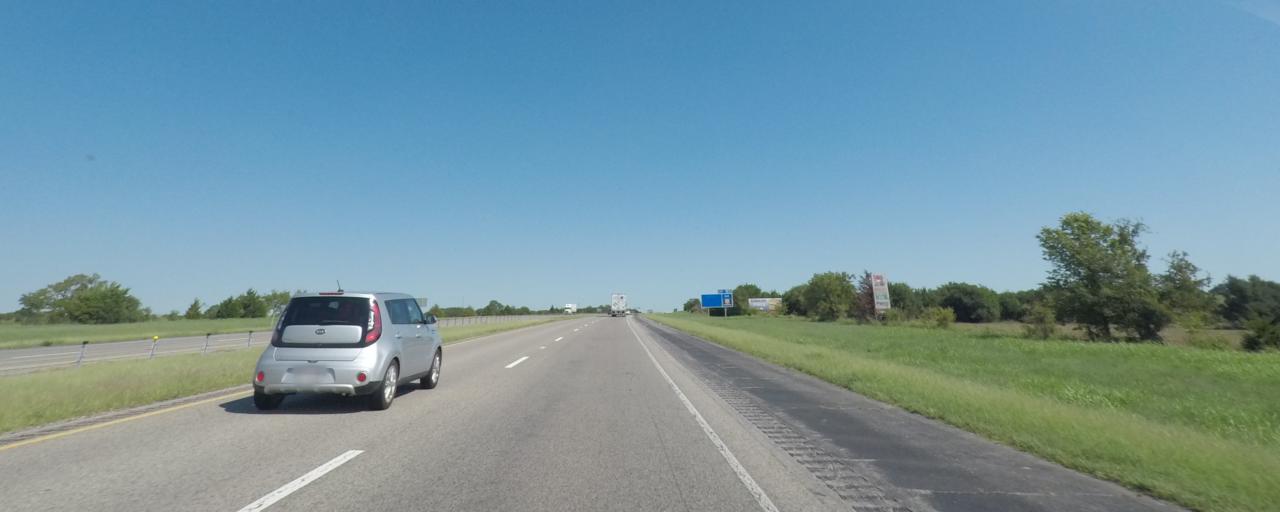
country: US
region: Oklahoma
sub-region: Noble County
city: Perry
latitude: 36.2617
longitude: -97.3267
